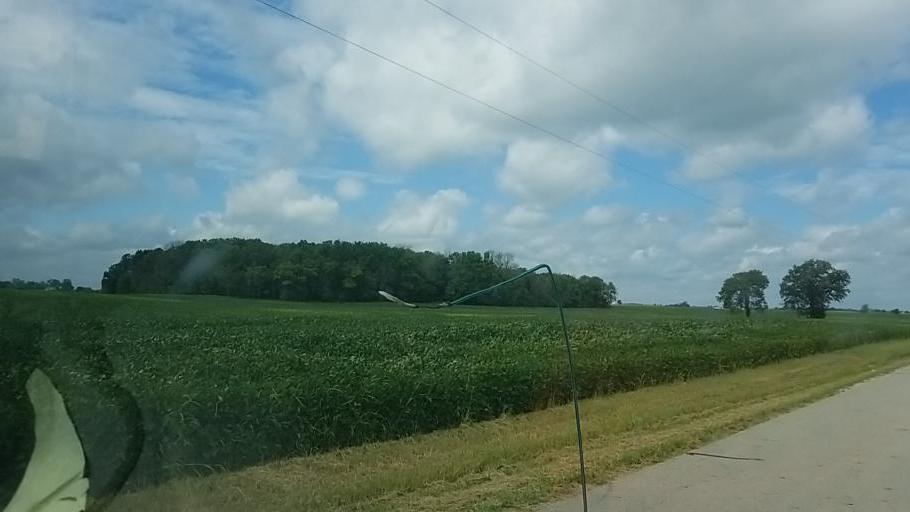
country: US
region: Ohio
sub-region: Fayette County
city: Jeffersonville
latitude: 39.6853
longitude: -83.5758
